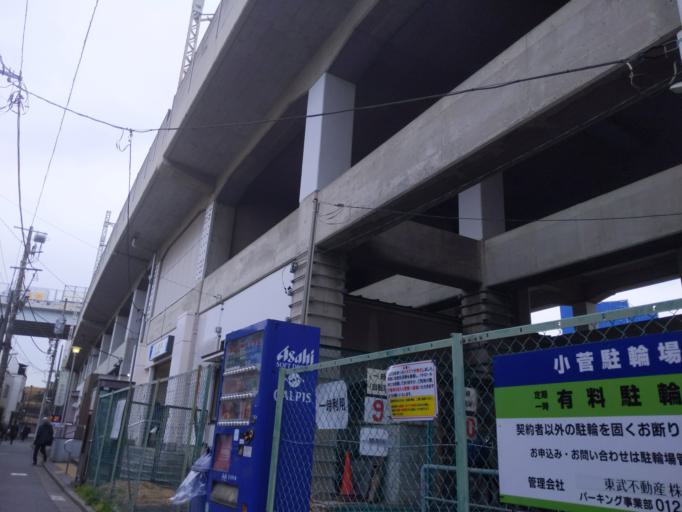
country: JP
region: Saitama
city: Soka
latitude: 35.7588
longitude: 139.8129
